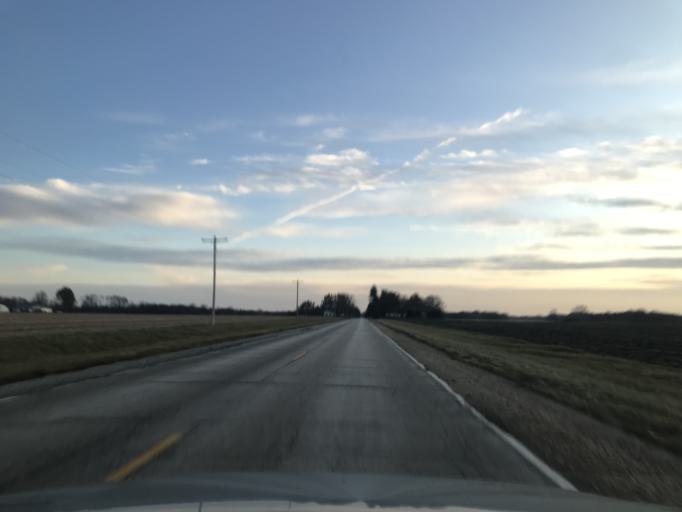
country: US
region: Illinois
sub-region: Henderson County
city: Oquawka
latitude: 40.9455
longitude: -90.8641
